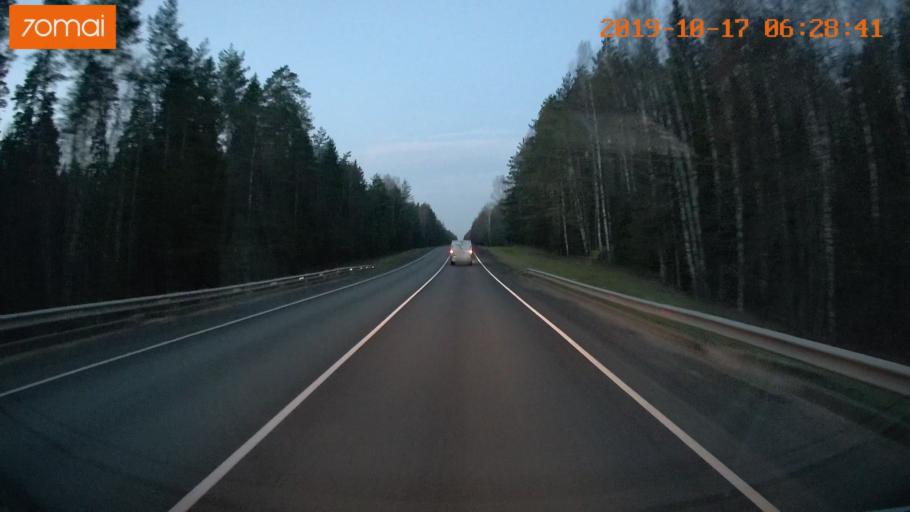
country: RU
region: Ivanovo
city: Lezhnevo
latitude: 56.7513
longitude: 40.7597
